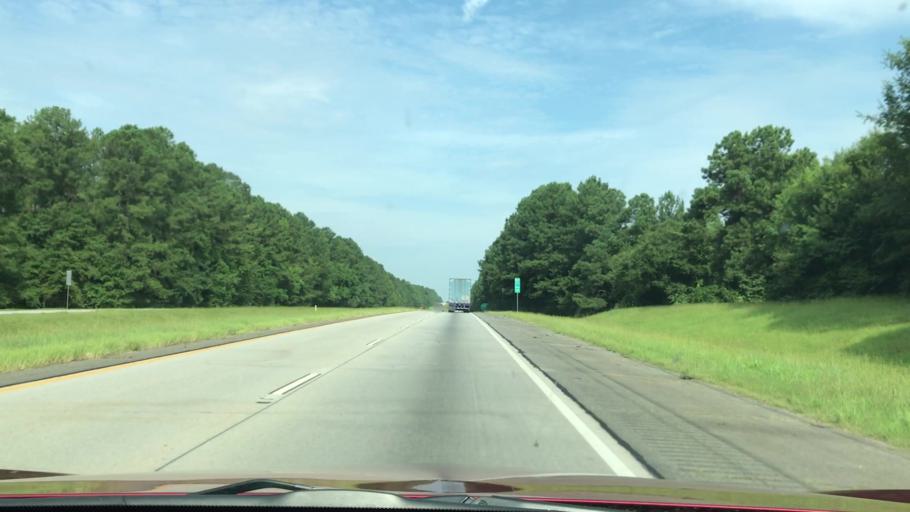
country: US
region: Georgia
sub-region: Warren County
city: Firing Range
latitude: 33.4967
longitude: -82.6892
